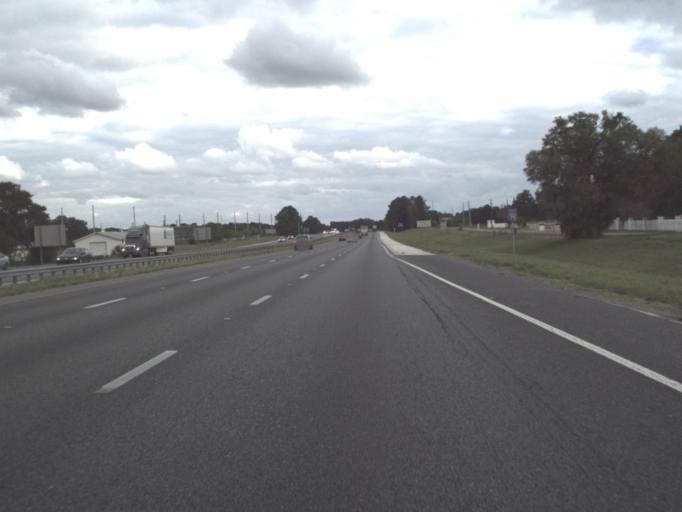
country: US
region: Florida
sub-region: Marion County
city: Belleview
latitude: 29.0195
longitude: -82.1559
